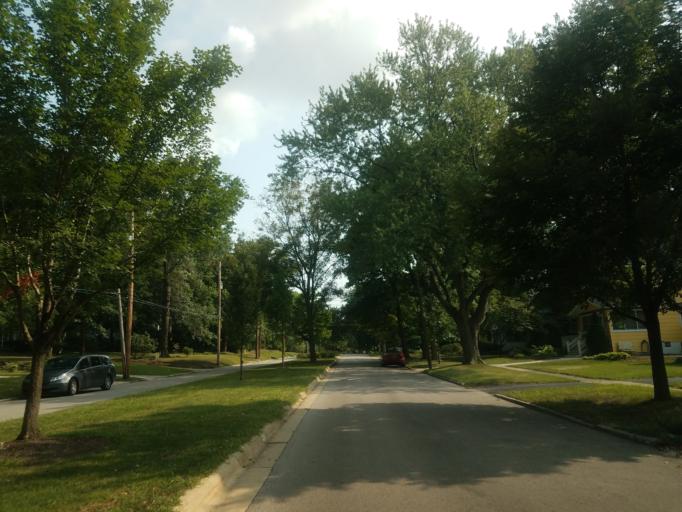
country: US
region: Illinois
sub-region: McLean County
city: Normal
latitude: 40.5018
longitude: -88.9856
